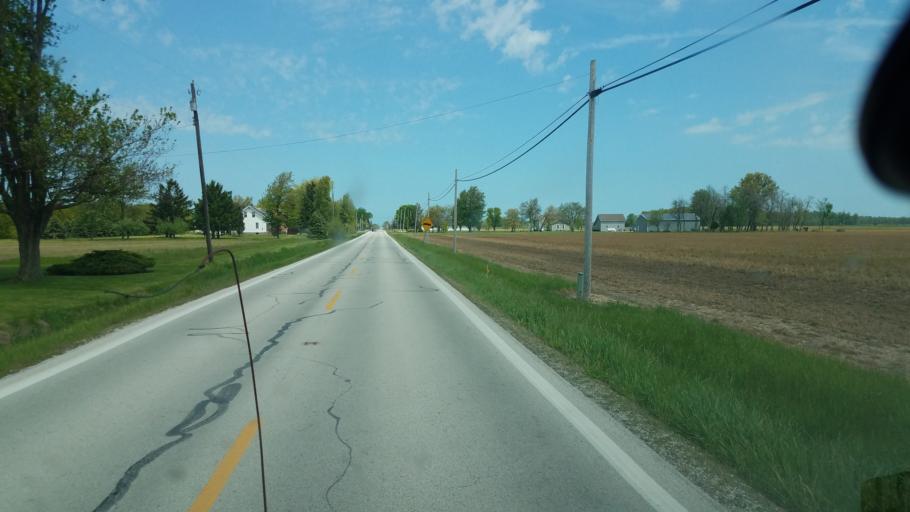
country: US
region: Ohio
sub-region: Ottawa County
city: Oak Harbor
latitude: 41.5638
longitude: -83.1450
